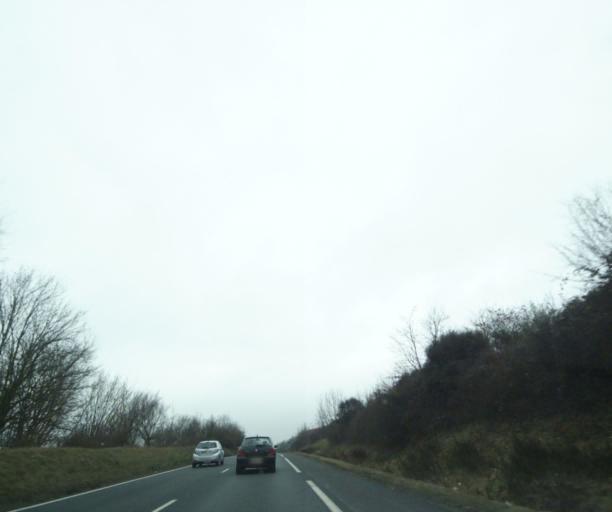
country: FR
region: Ile-de-France
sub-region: Departement de l'Essonne
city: Champlan
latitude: 48.7079
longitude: 2.2904
